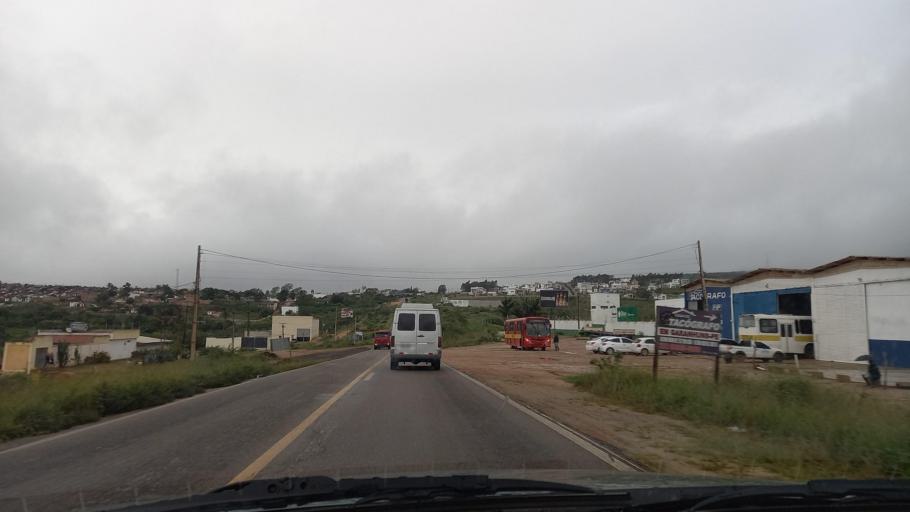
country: BR
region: Pernambuco
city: Garanhuns
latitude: -8.8603
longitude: -36.5112
